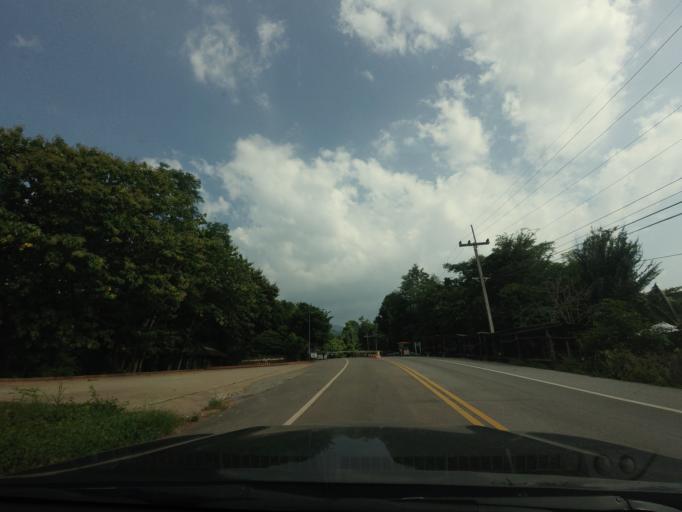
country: TH
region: Phitsanulok
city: Nakhon Thai
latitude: 17.0232
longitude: 100.9366
